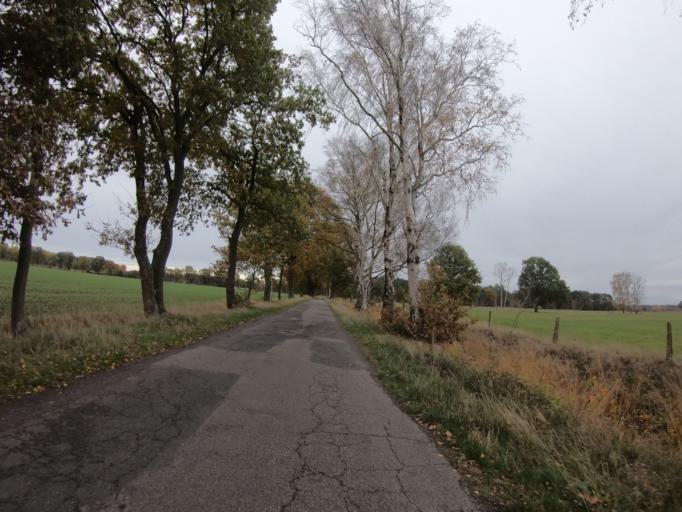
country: DE
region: Lower Saxony
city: Gifhorn
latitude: 52.4738
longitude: 10.5878
